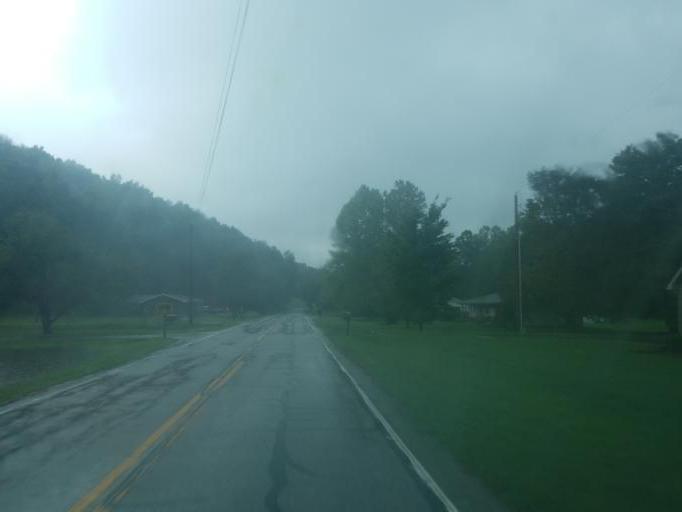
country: US
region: Kentucky
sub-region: Carter County
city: Olive Hill
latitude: 38.2861
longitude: -83.2978
